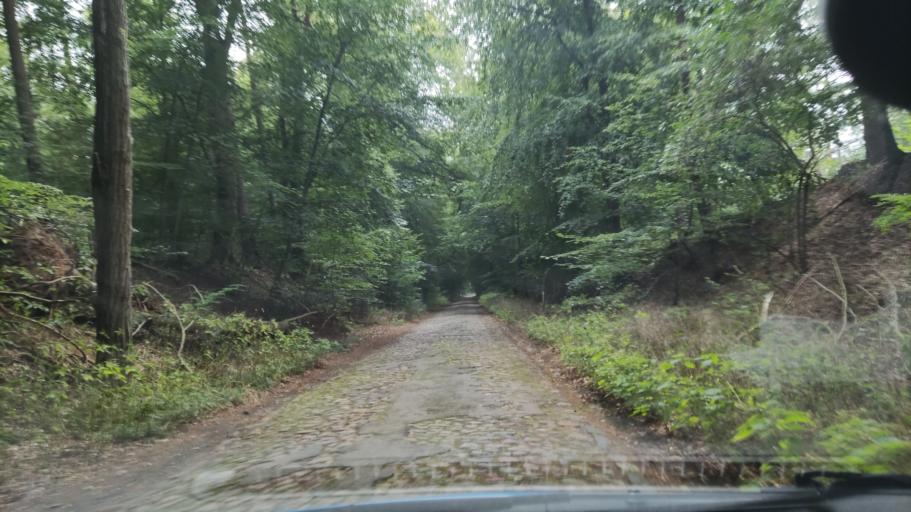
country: DE
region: Lower Saxony
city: Altenmedingen
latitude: 53.1490
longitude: 10.5844
